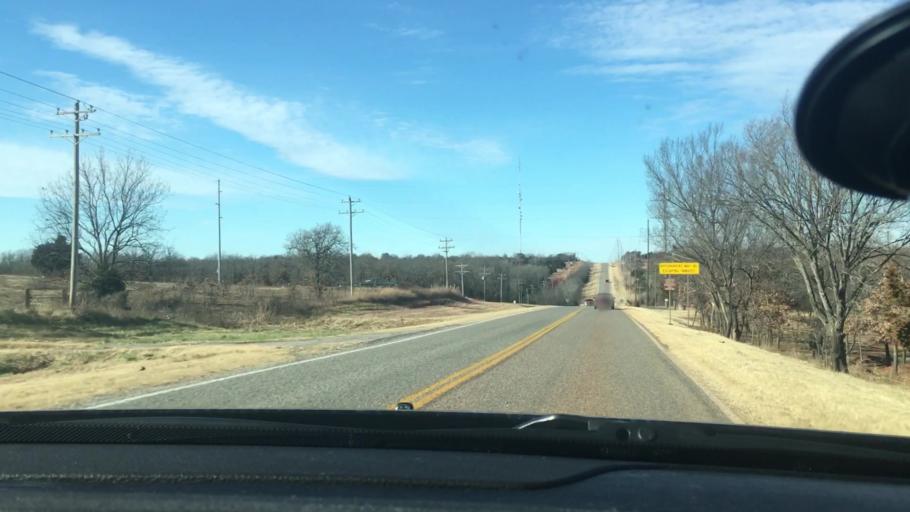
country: US
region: Oklahoma
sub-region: Cleveland County
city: Lexington
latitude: 35.0150
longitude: -97.1755
